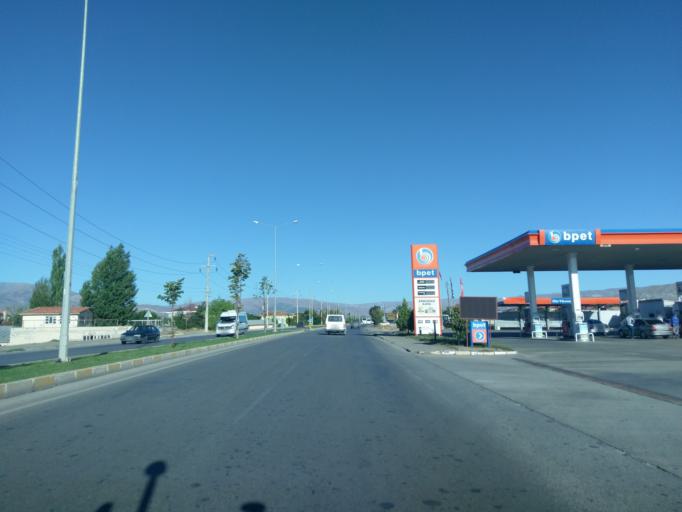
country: TR
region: Erzincan
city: Erzincan
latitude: 39.7509
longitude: 39.4579
